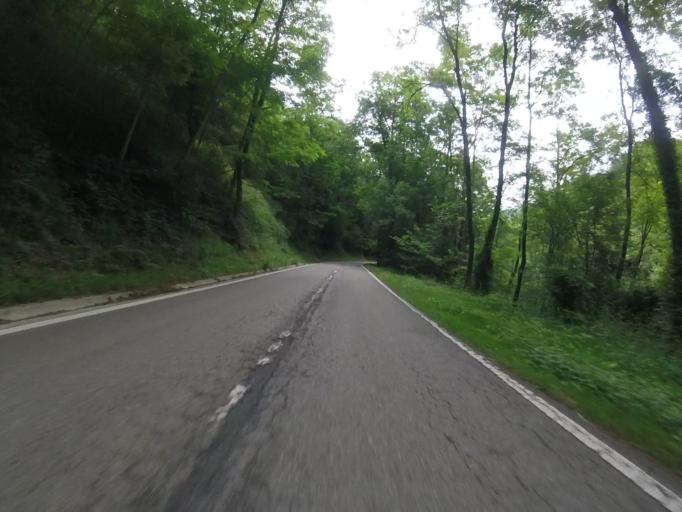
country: ES
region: Navarre
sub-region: Provincia de Navarra
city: Zubieta
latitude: 43.1262
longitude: -1.7481
